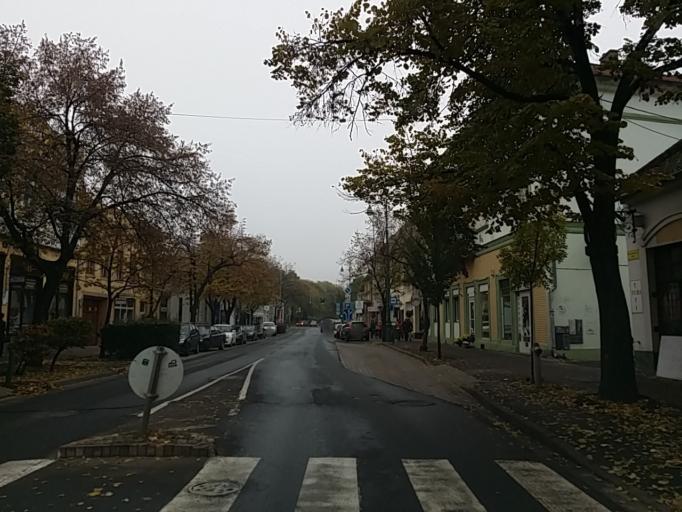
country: HU
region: Heves
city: Gyongyos
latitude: 47.7851
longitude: 19.9293
